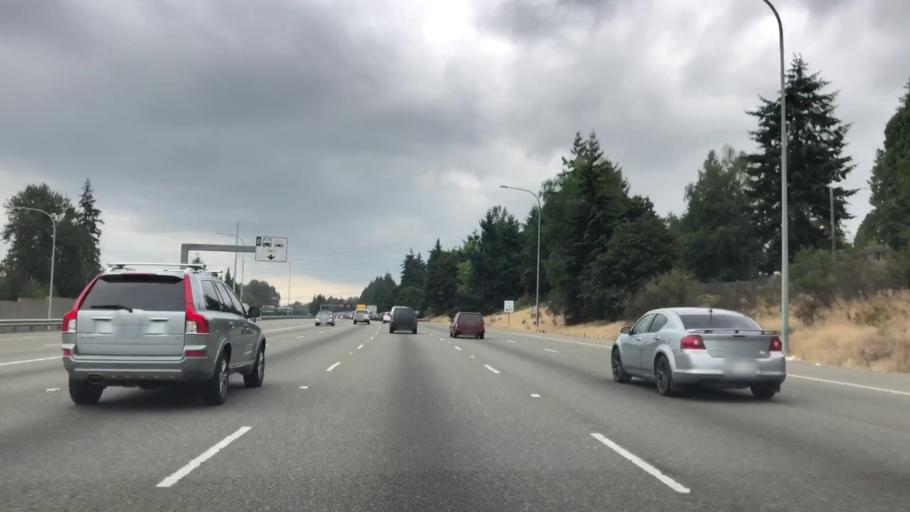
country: US
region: Washington
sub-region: Snohomish County
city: Everett
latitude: 47.9510
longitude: -122.1998
